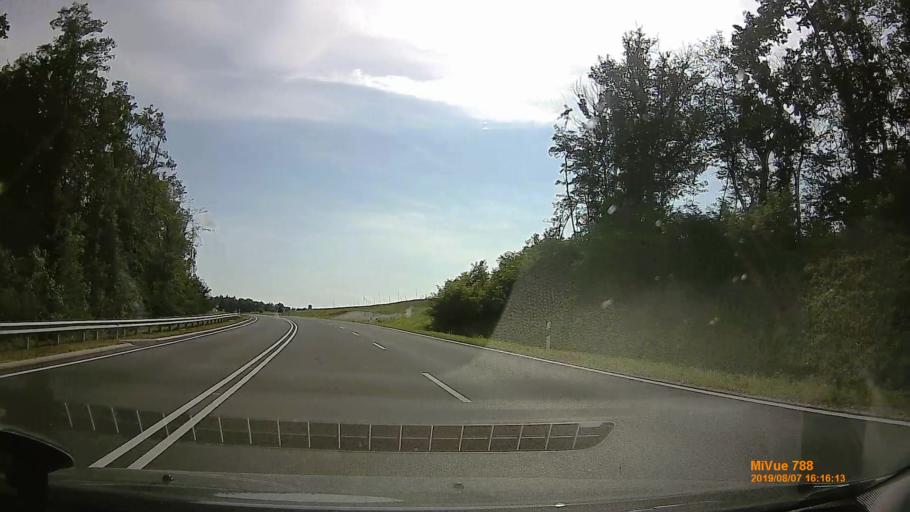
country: HU
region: Zala
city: Zalalovo
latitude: 46.8226
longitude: 16.5831
